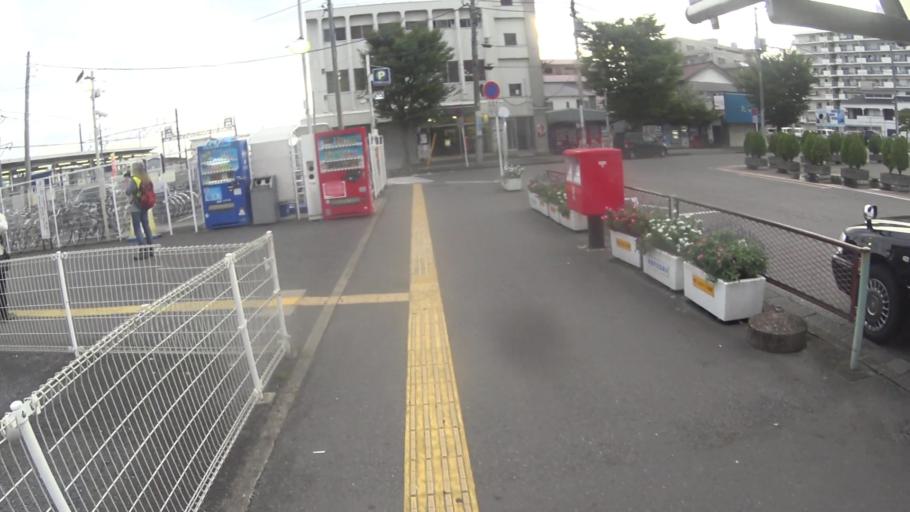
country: JP
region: Saitama
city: Iwatsuki
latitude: 35.9637
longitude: 139.7123
